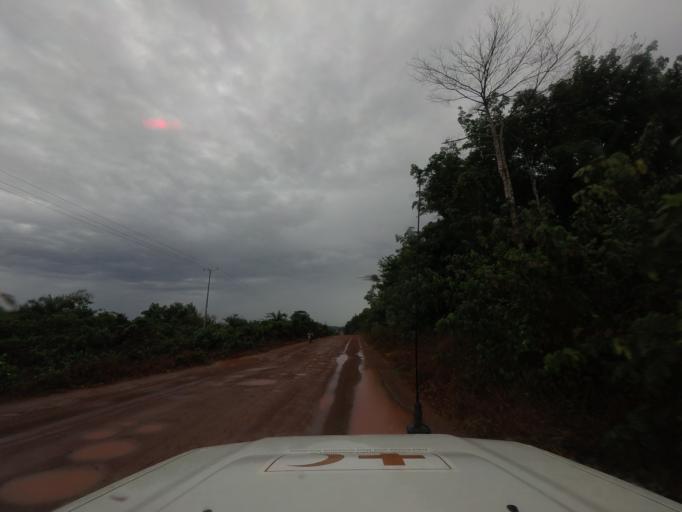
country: LR
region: Nimba
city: Sanniquellie
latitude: 7.2297
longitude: -8.9484
